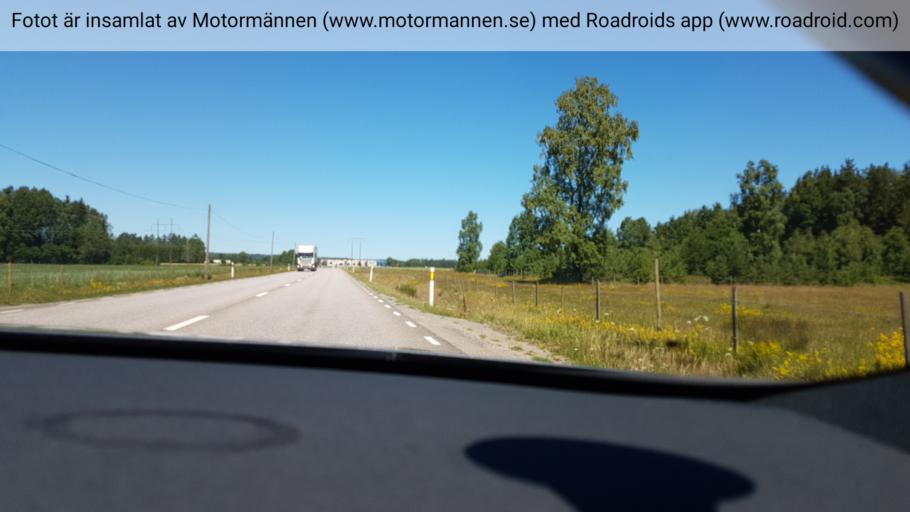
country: SE
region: Vaestra Goetaland
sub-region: Ulricehamns Kommun
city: Ulricehamn
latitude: 57.8347
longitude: 13.4380
